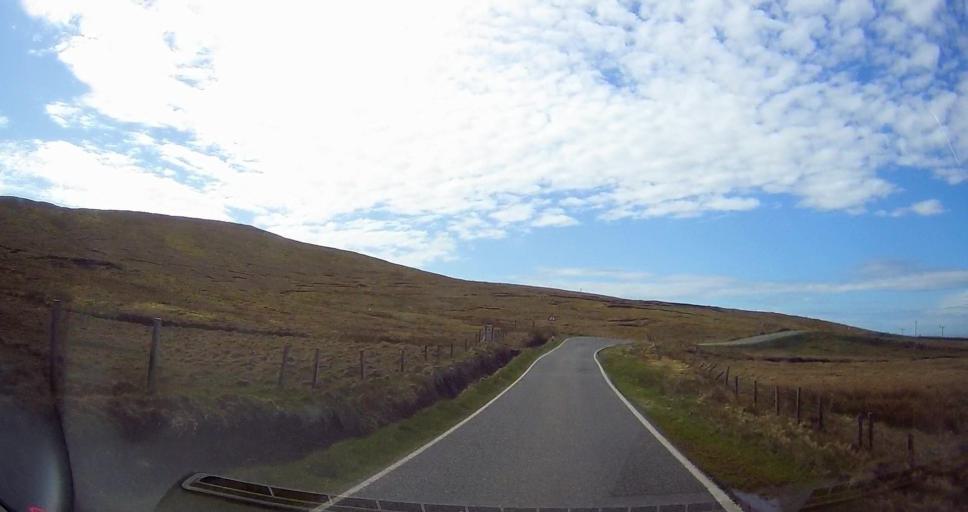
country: GB
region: Scotland
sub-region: Shetland Islands
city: Sandwick
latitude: 59.9814
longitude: -1.2919
